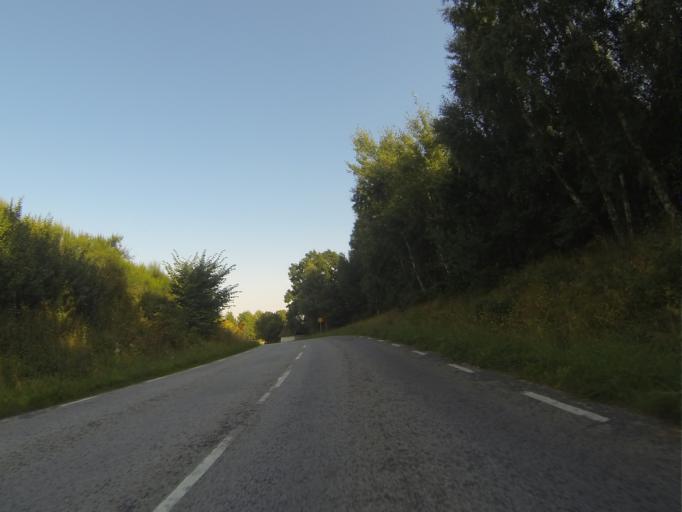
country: SE
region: Skane
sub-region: Lunds Kommun
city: Genarp
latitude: 55.5816
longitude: 13.3395
